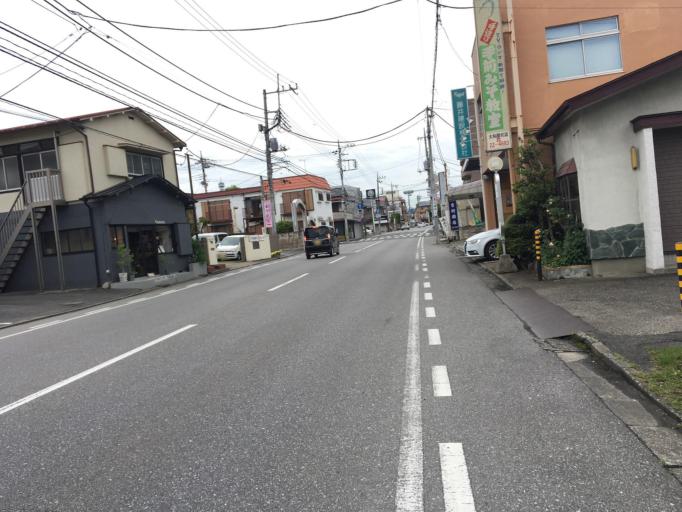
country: JP
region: Tochigi
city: Utsunomiya-shi
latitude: 36.5697
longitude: 139.8736
